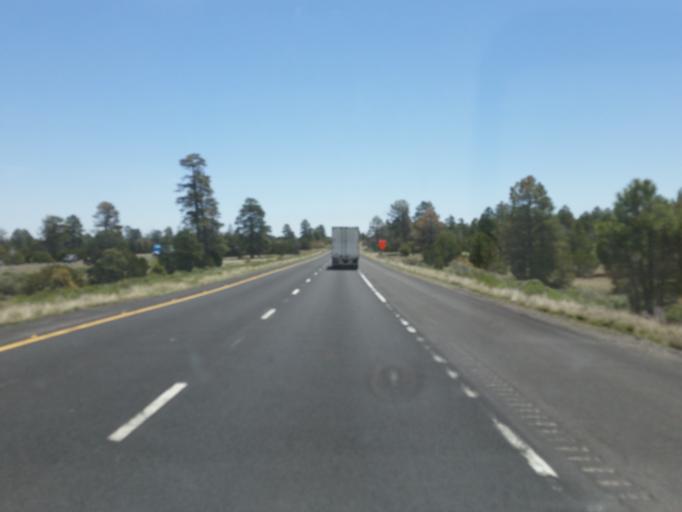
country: US
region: Arizona
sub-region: Coconino County
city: Flagstaff
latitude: 35.2107
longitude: -111.5268
